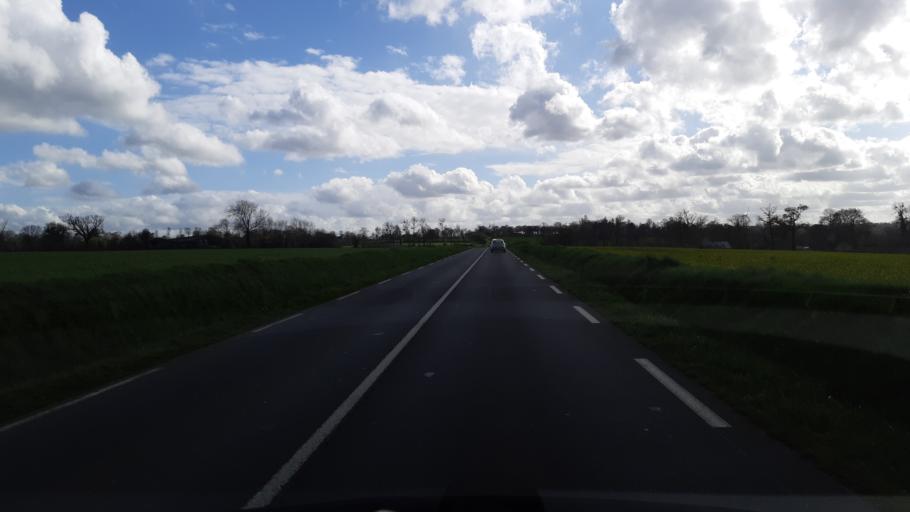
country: FR
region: Lower Normandy
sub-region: Departement de la Manche
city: Agneaux
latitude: 49.0399
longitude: -1.1312
